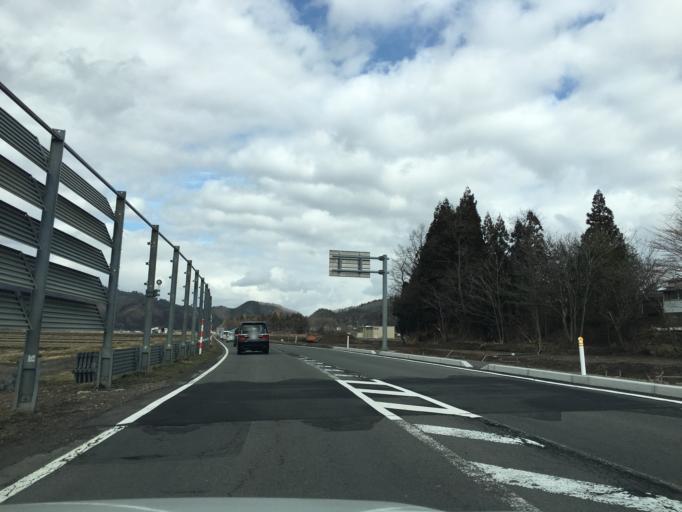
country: JP
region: Akita
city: Hanawa
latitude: 40.2292
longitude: 140.7315
